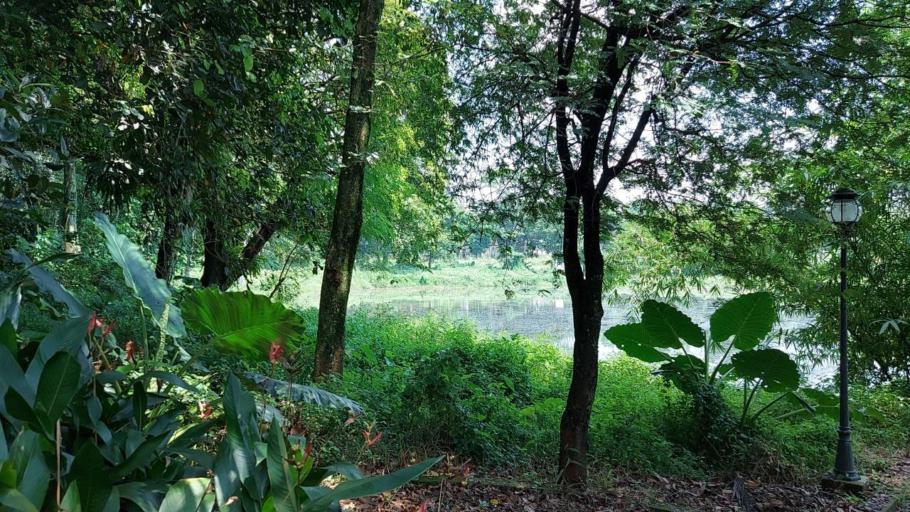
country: ID
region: West Java
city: Cibinong
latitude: -6.4917
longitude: 106.8516
